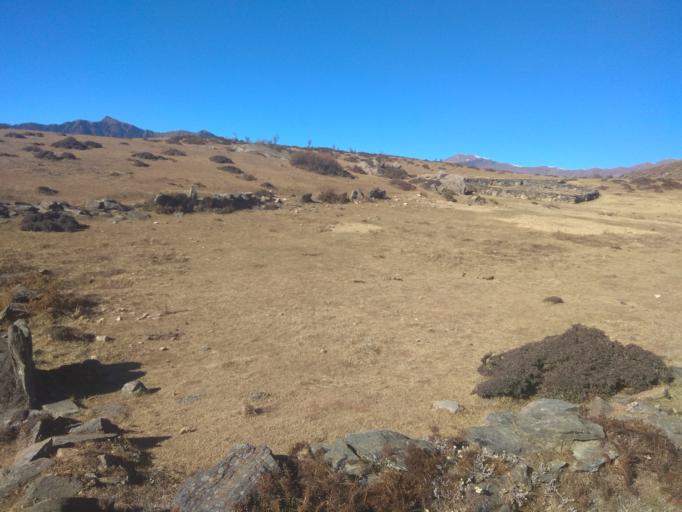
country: NP
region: Far Western
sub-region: Seti Zone
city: Achham
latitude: 29.2807
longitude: 81.6462
